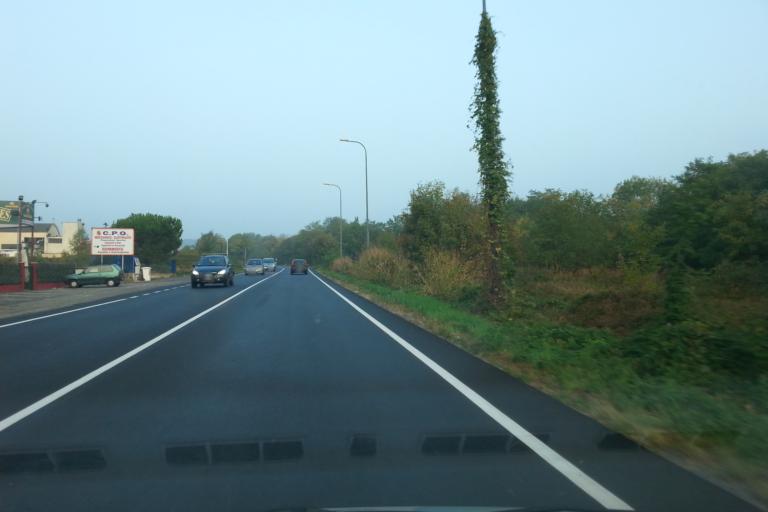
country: IT
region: Piedmont
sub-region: Provincia di Torino
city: Trana
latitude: 45.0330
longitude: 7.4352
